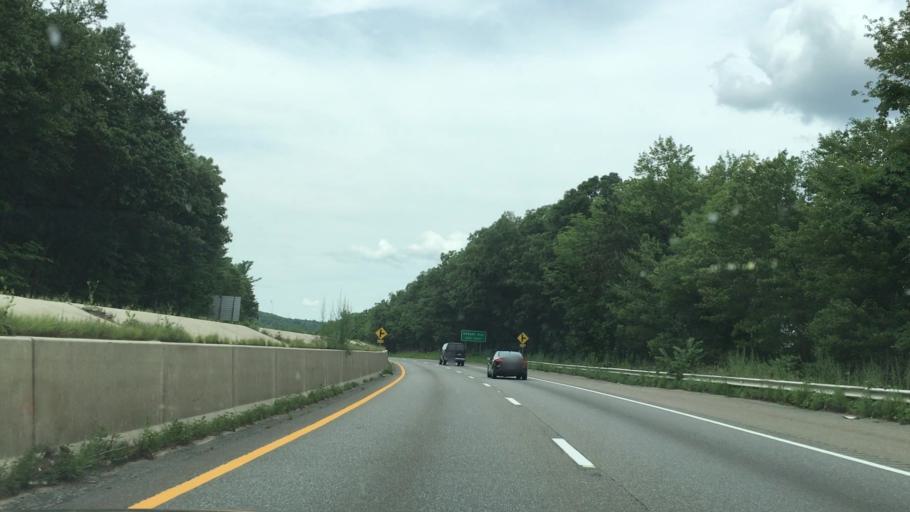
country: US
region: Massachusetts
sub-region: Worcester County
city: Leominster
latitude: 42.5524
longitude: -71.7711
